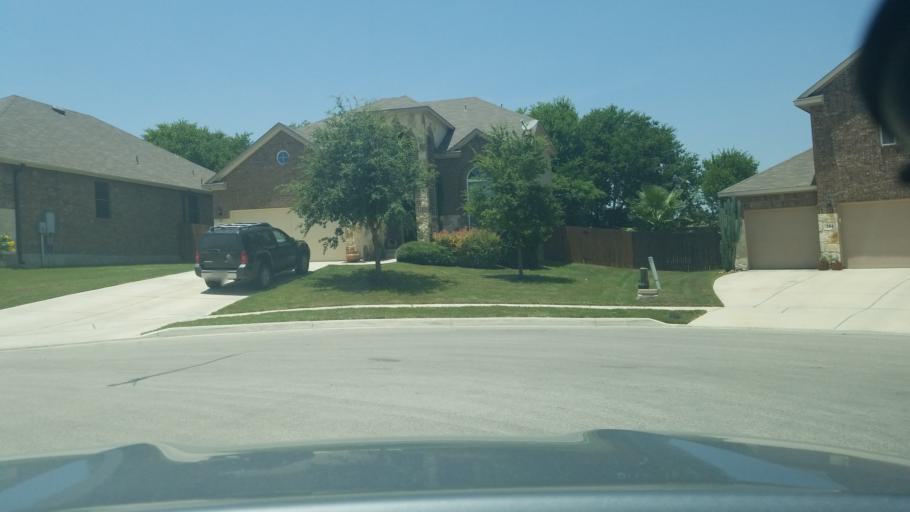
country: US
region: Texas
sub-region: Guadalupe County
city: Cibolo
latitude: 29.5821
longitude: -98.2277
